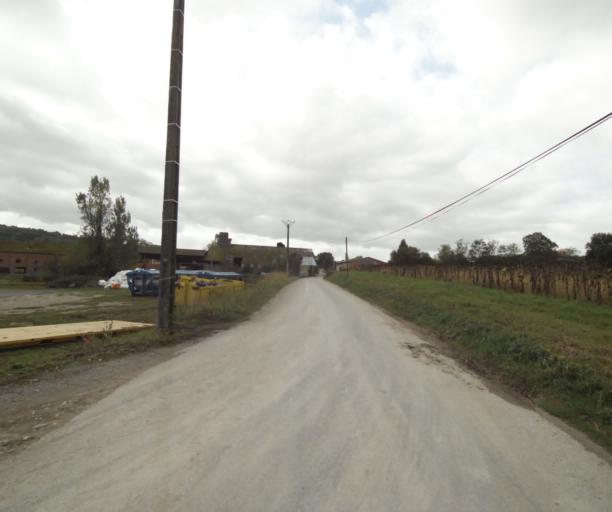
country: FR
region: Midi-Pyrenees
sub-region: Departement du Tarn-et-Garonne
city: Beaumont-de-Lomagne
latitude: 43.8633
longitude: 1.1024
